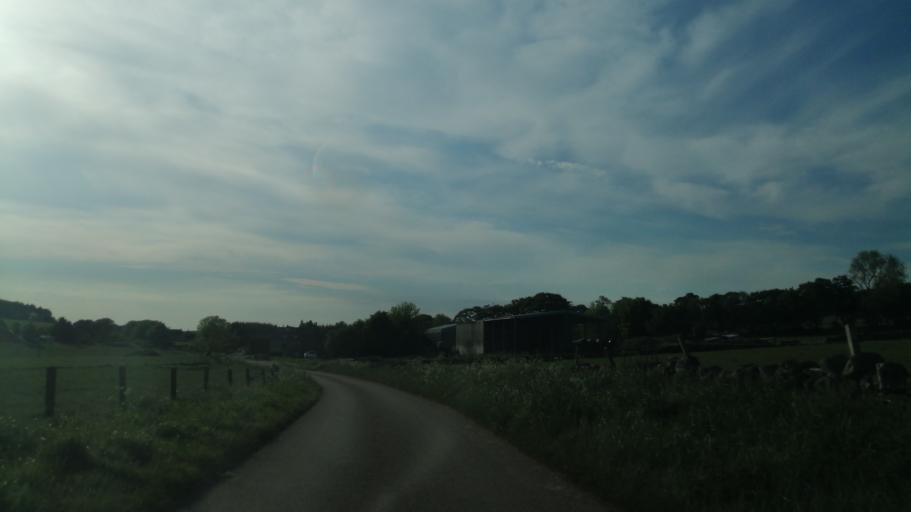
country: GB
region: Scotland
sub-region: Moray
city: Cullen
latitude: 57.5743
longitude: -2.7843
